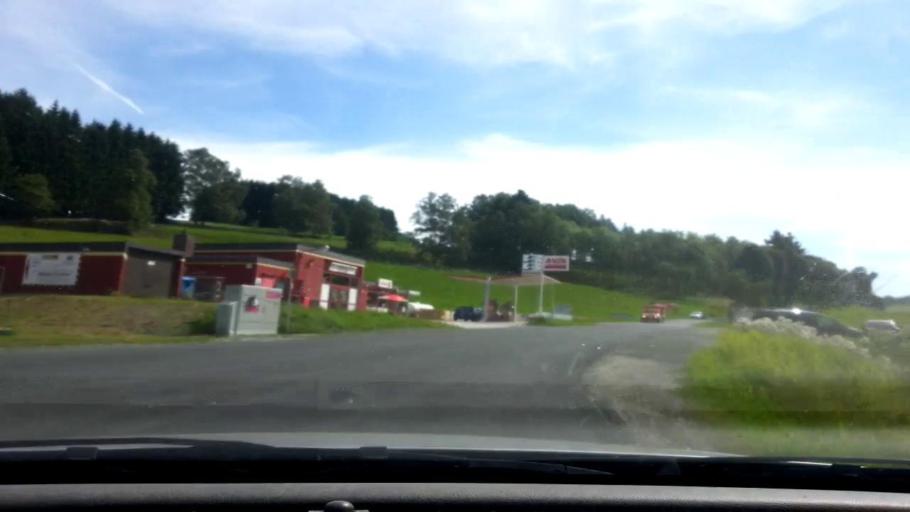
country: DE
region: Bavaria
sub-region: Upper Franconia
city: Bischofsgrun
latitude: 50.0555
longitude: 11.7812
